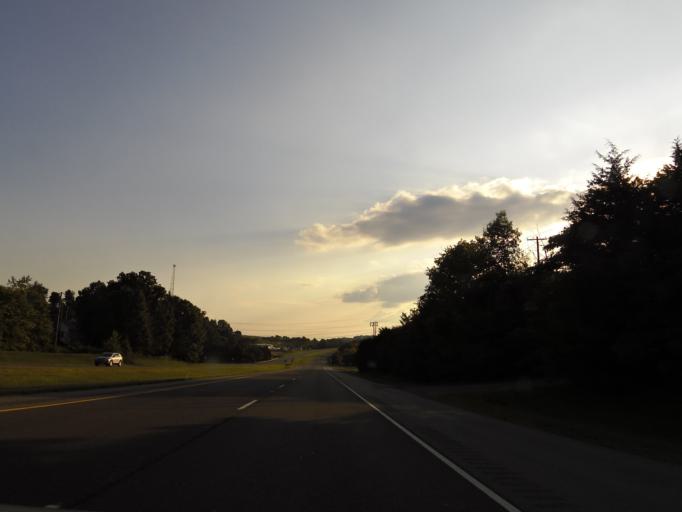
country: US
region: Tennessee
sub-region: Knox County
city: Mascot
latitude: 36.0516
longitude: -83.7995
